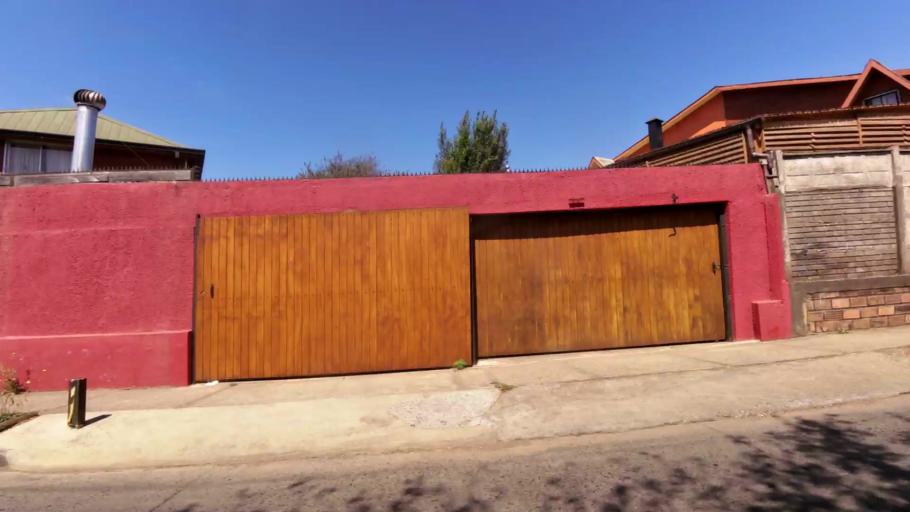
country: CL
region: Biobio
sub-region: Provincia de Concepcion
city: Concepcion
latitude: -36.7833
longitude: -73.0423
